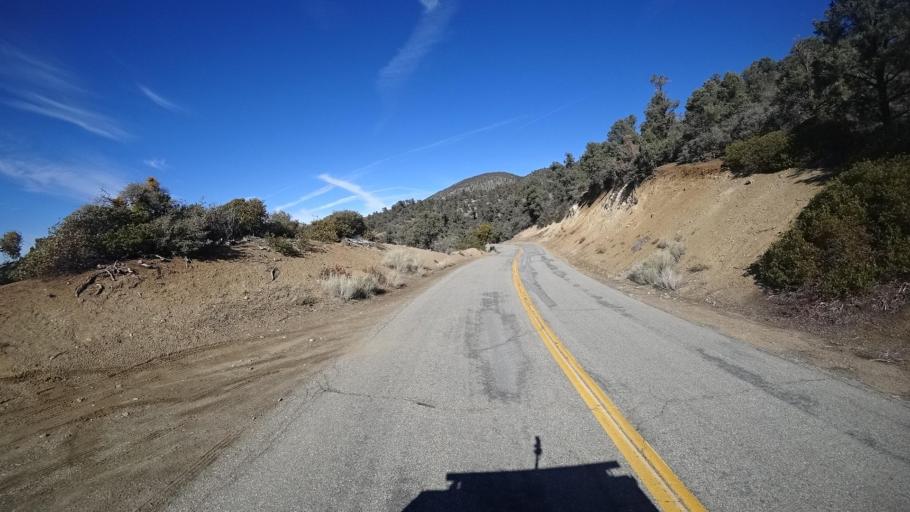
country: US
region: California
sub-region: Kern County
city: Pine Mountain Club
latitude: 34.8639
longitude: -119.2296
